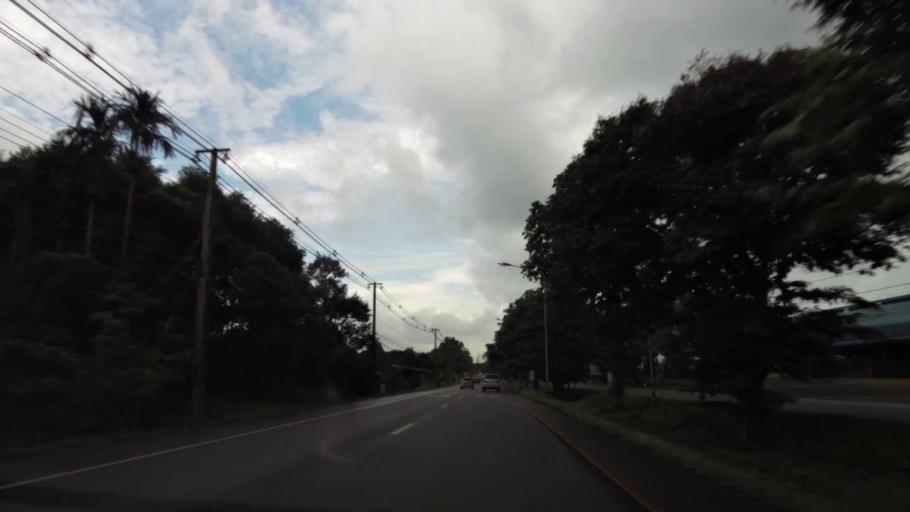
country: TH
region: Chanthaburi
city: Khlung
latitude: 12.4812
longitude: 102.1830
